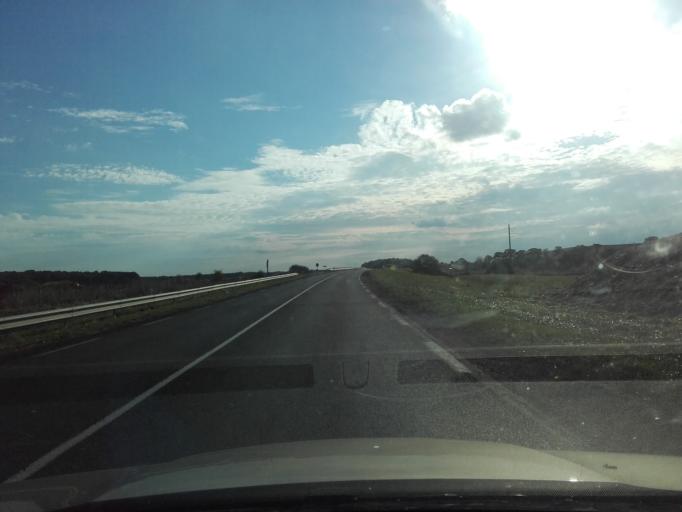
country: FR
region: Centre
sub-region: Departement d'Indre-et-Loire
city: Parcay-Meslay
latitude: 47.4760
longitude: 0.7589
